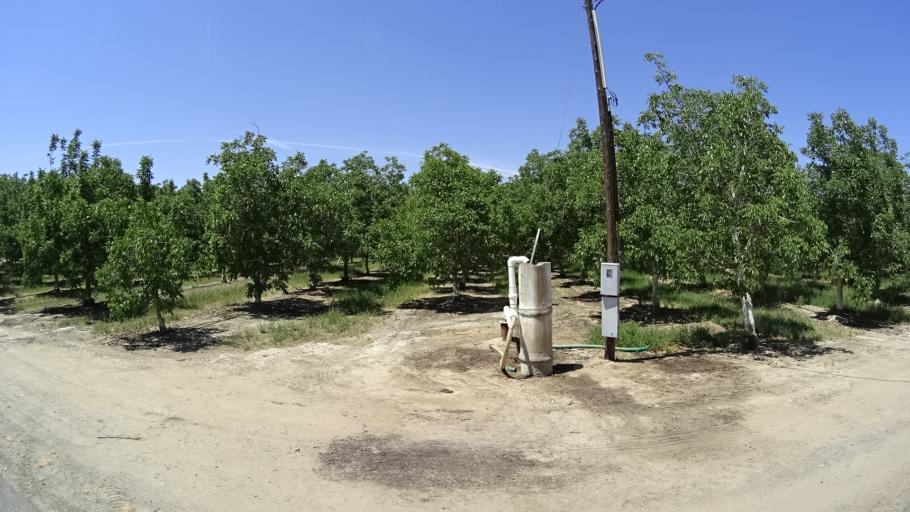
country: US
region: California
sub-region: Kings County
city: Armona
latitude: 36.2485
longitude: -119.6910
